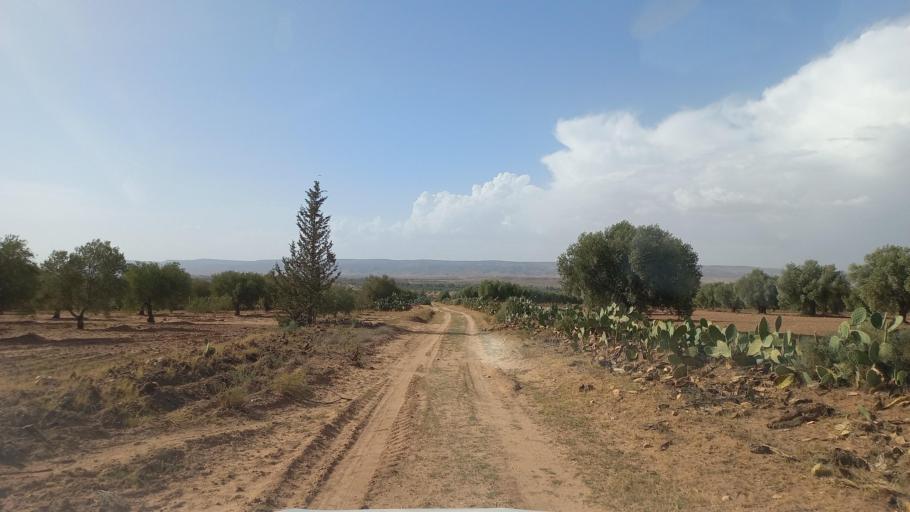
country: TN
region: Al Qasrayn
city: Kasserine
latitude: 35.2108
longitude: 8.9543
